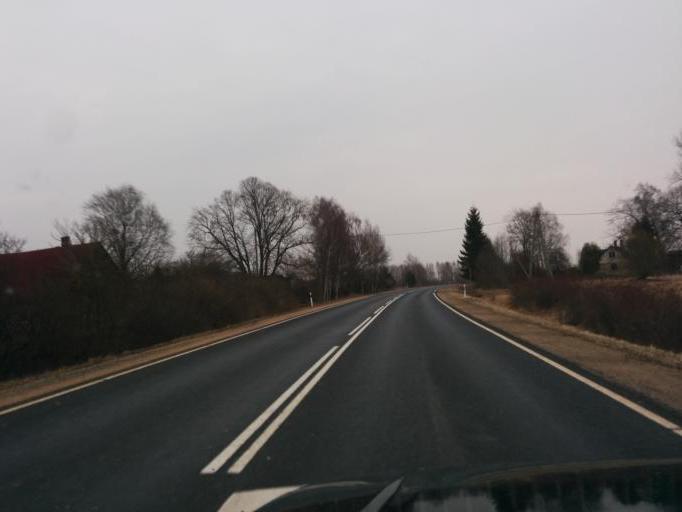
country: LV
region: Salaspils
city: Salaspils
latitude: 56.8260
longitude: 24.3167
